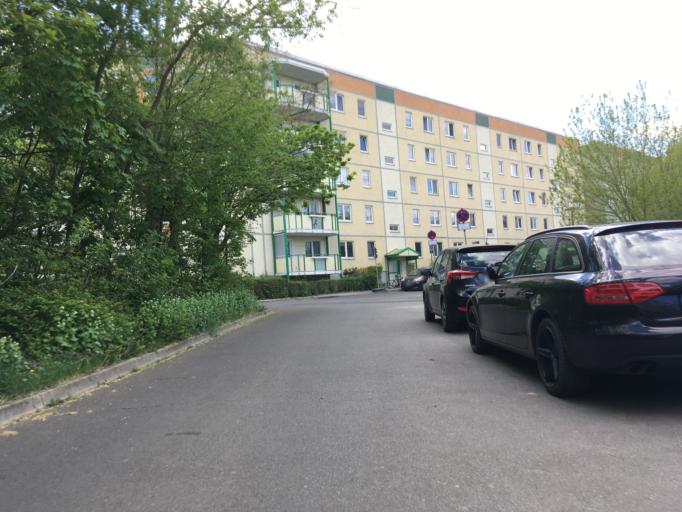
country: DE
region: Berlin
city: Hellersdorf
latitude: 52.5378
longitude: 13.6242
